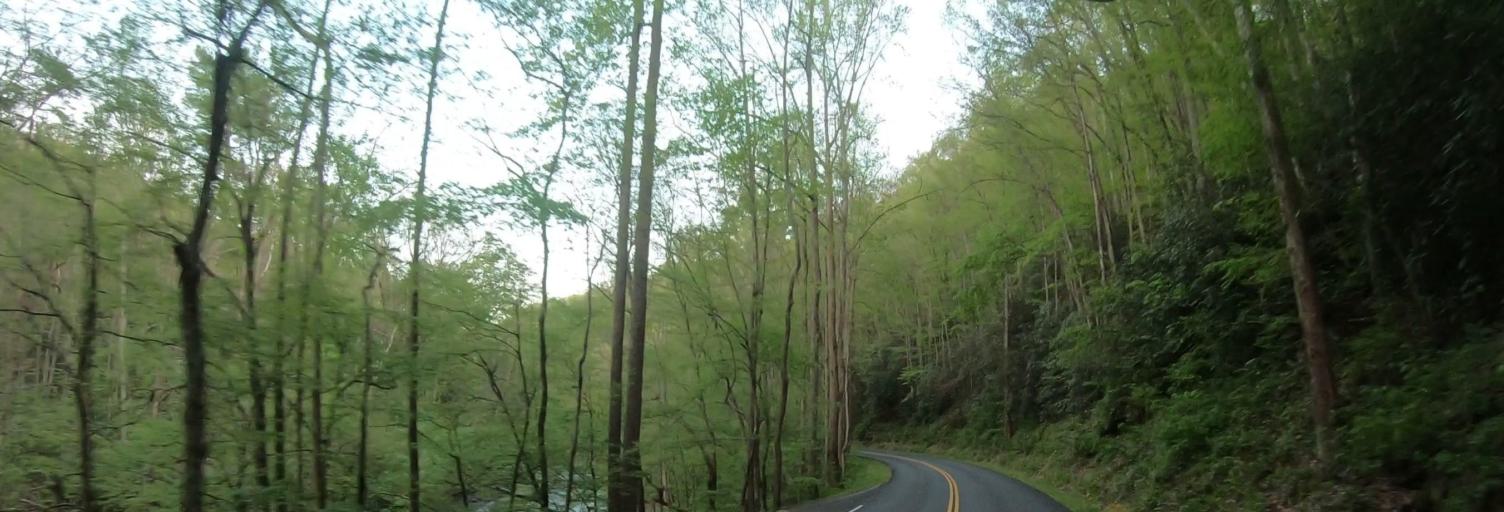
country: US
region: Tennessee
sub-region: Sevier County
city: Gatlinburg
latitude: 35.6733
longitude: -83.6457
